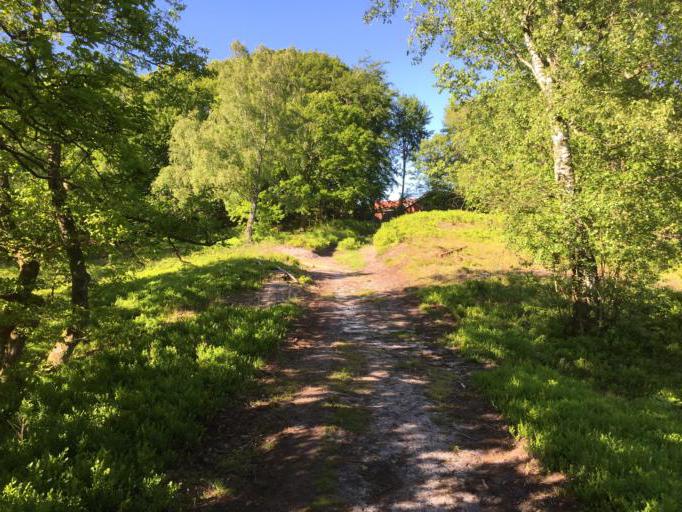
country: DK
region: Central Jutland
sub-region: Silkeborg Kommune
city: Svejbaek
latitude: 56.2196
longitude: 9.6950
